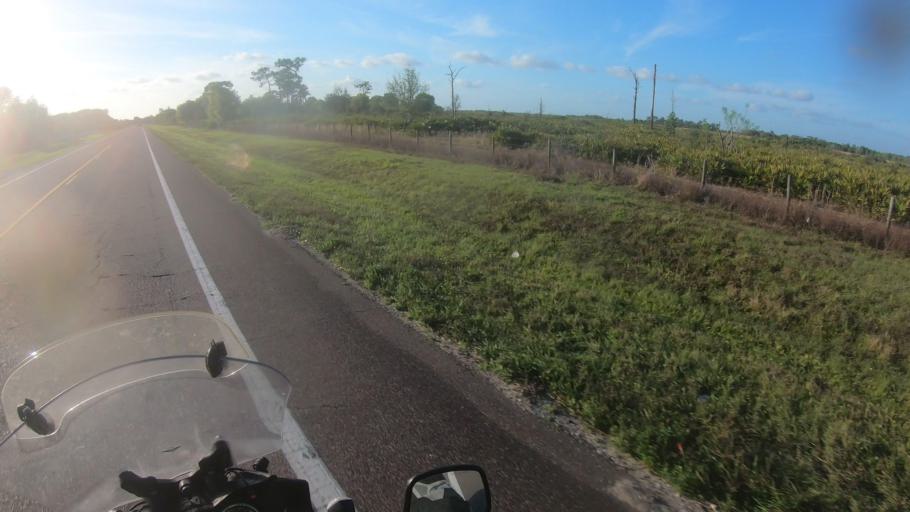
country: US
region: Florida
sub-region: DeSoto County
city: Arcadia
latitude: 27.2952
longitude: -82.0650
